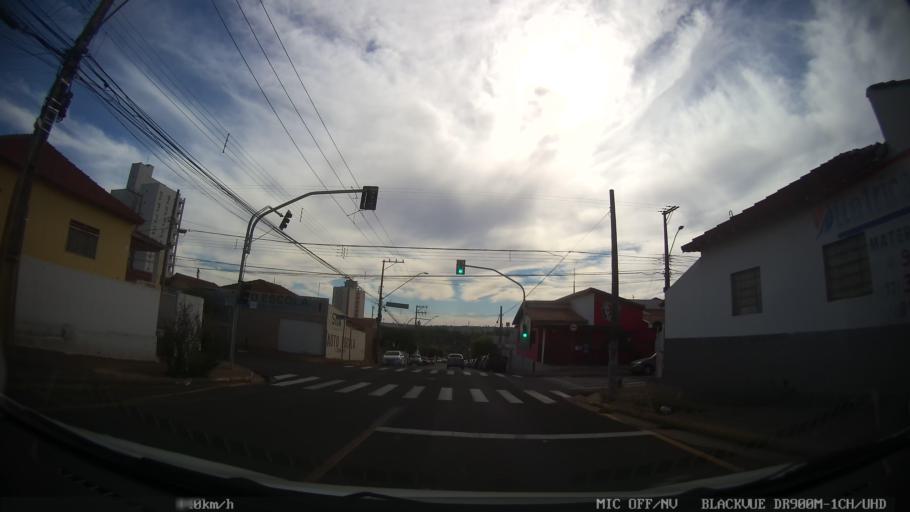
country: BR
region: Sao Paulo
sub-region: Catanduva
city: Catanduva
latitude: -21.1345
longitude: -48.9790
